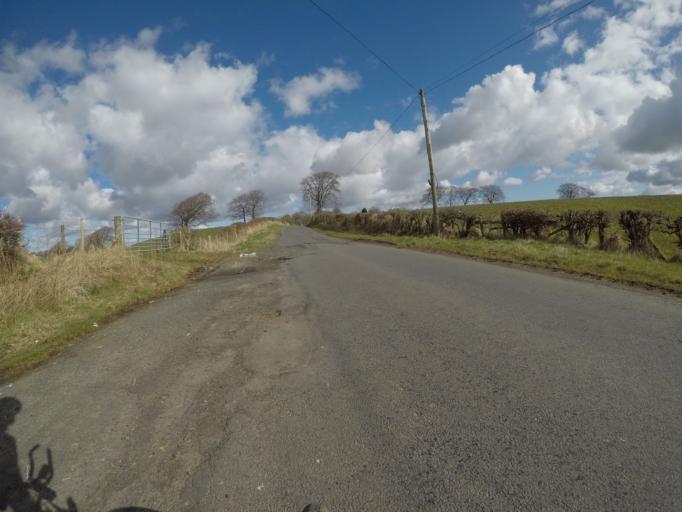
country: GB
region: Scotland
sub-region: North Ayrshire
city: Beith
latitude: 55.7165
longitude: -4.6204
